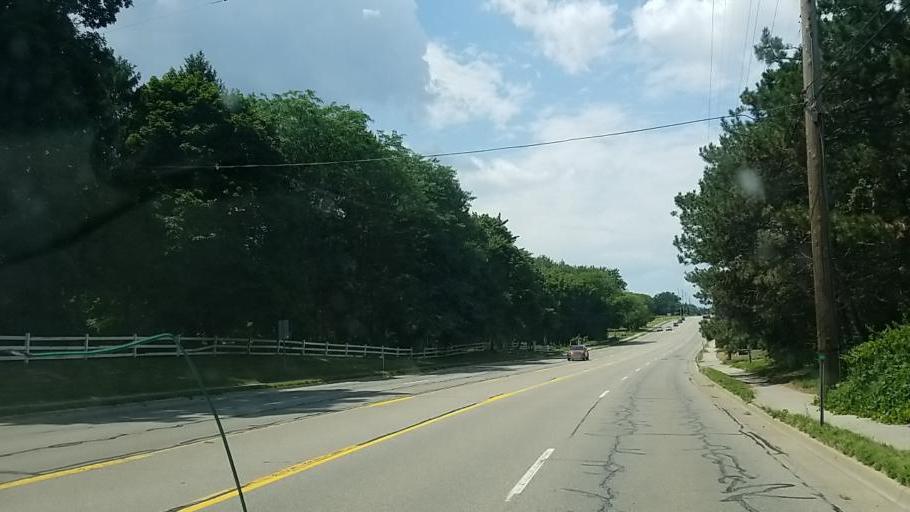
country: US
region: Michigan
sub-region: Kent County
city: East Grand Rapids
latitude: 42.9610
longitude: -85.5666
